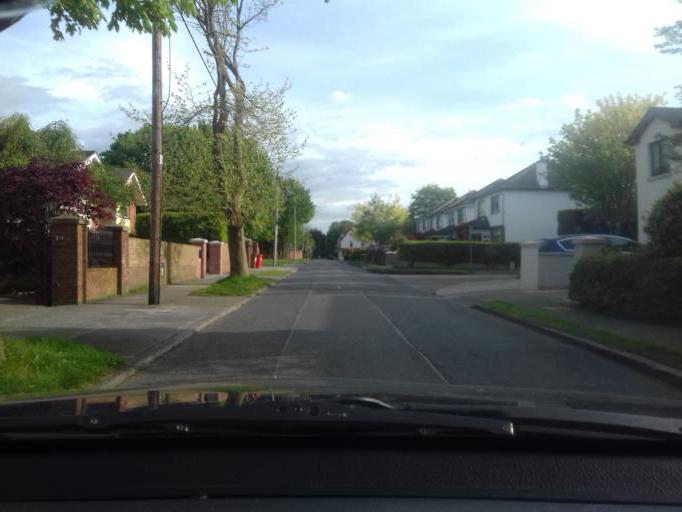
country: IE
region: Leinster
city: Castleknock
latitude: 53.3739
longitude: -6.3561
